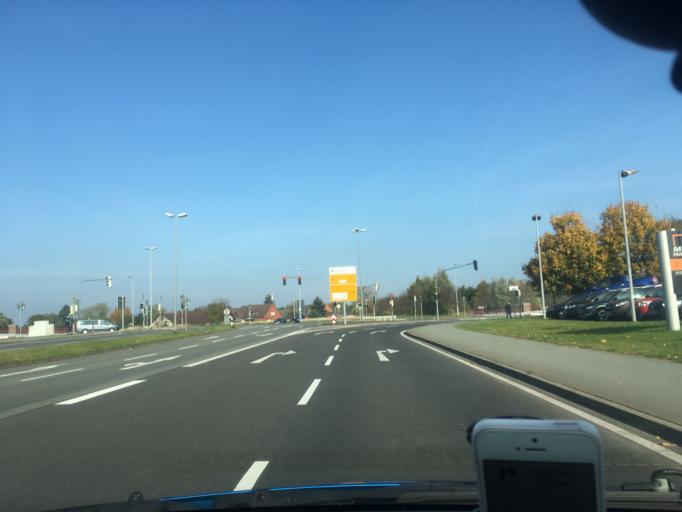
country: DE
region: Mecklenburg-Vorpommern
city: Feldstadt
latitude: 53.5919
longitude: 11.4048
